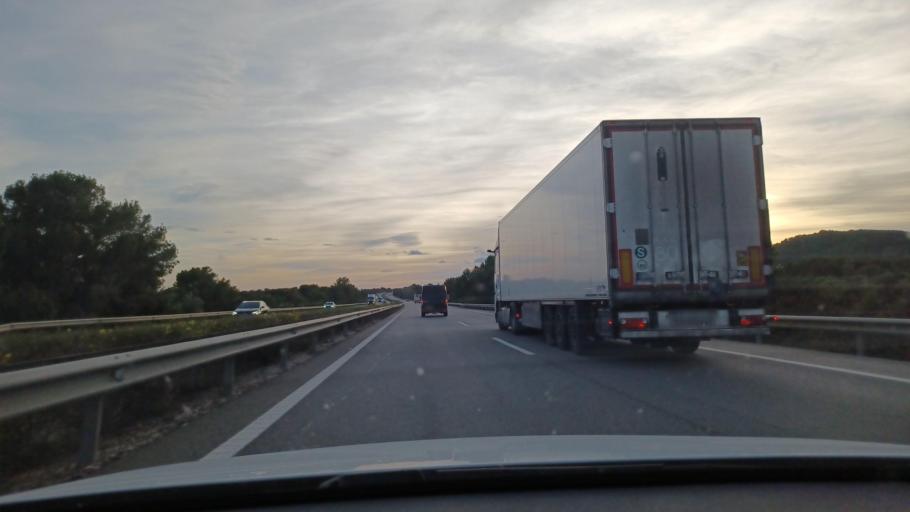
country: ES
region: Catalonia
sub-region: Provincia de Tarragona
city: l'Ametlla de Mar
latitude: 40.8616
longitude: 0.7706
